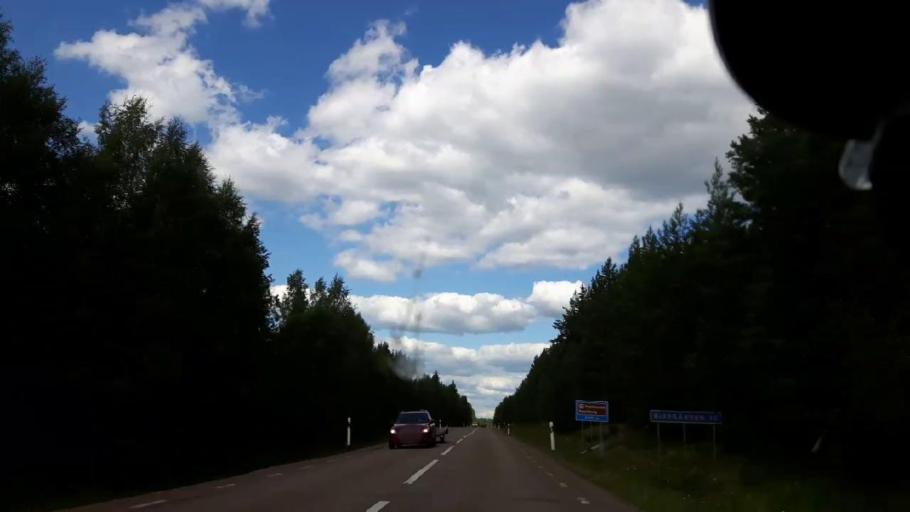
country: SE
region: Jaemtland
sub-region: Ragunda Kommun
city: Hammarstrand
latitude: 62.9237
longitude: 16.7021
